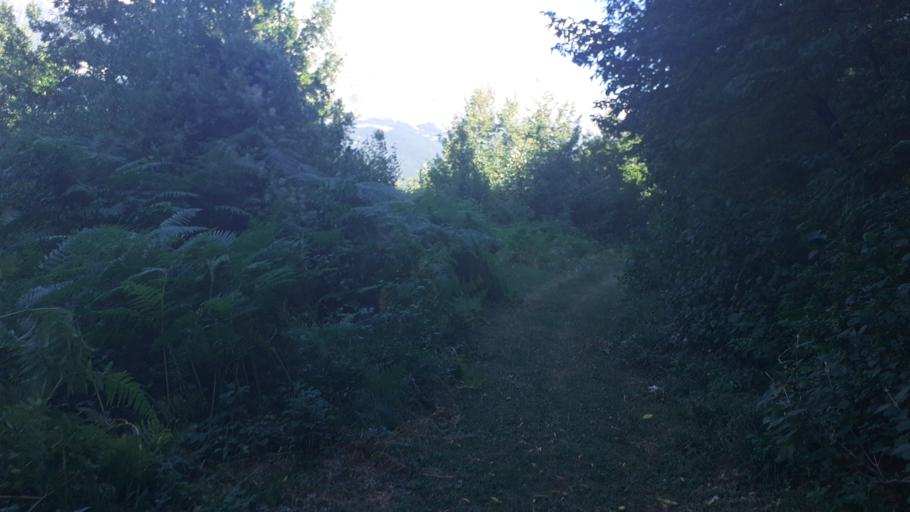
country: IT
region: Abruzzo
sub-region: Provincia di Pescara
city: Sant'Eufemia a Maiella
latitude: 42.1077
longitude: 14.0014
